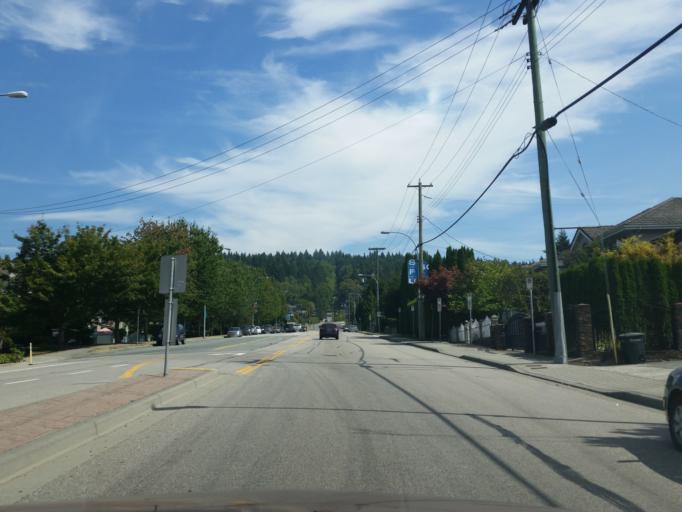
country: CA
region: British Columbia
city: Burnaby
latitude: 49.2804
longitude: -122.9573
